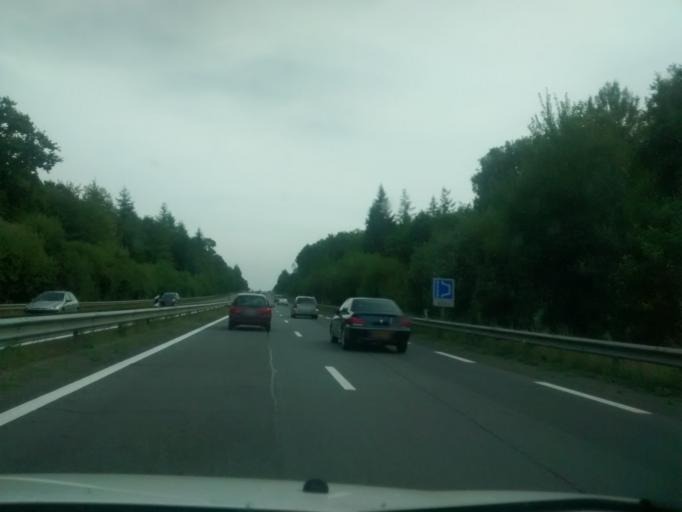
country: FR
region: Brittany
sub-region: Departement d'Ille-et-Vilaine
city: Miniac-Morvan
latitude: 48.5057
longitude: -1.9095
